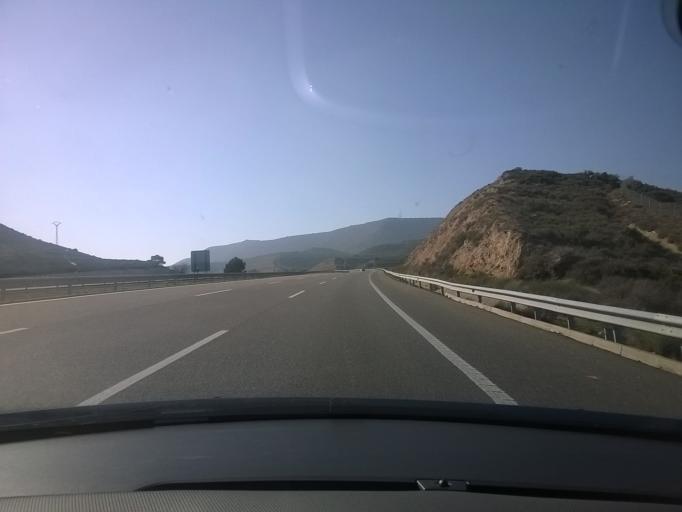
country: ES
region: Aragon
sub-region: Provincia de Huesca
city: Fraga
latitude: 41.4834
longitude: 0.3235
